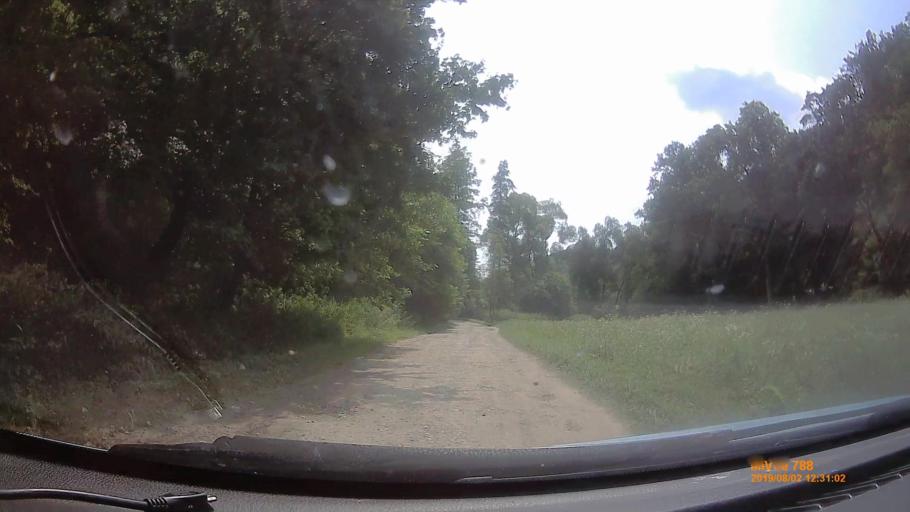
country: HU
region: Baranya
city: Buekkoesd
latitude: 46.1070
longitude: 17.9358
